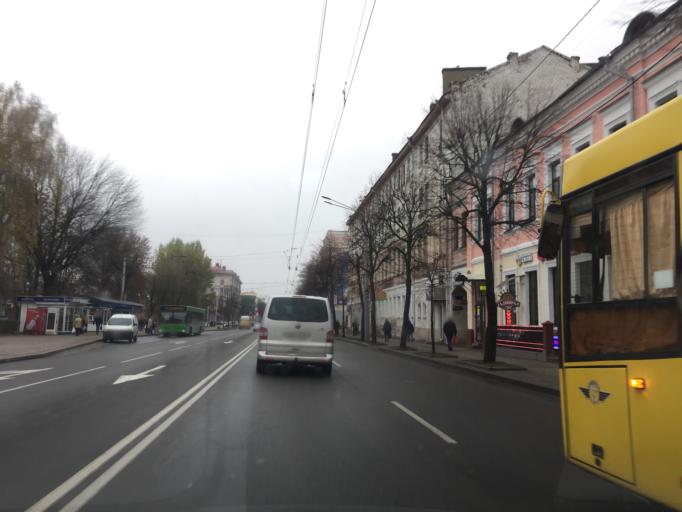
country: BY
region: Mogilev
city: Mahilyow
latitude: 53.8998
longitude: 30.3342
